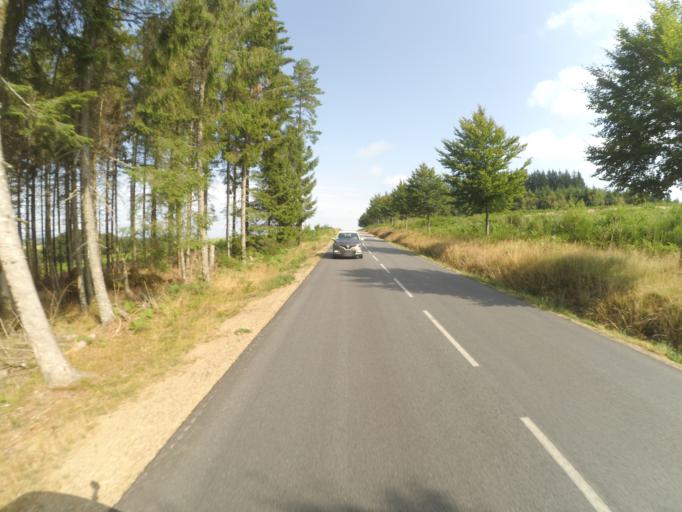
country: FR
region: Limousin
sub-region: Departement de la Correze
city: Meymac
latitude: 45.6097
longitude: 2.1094
